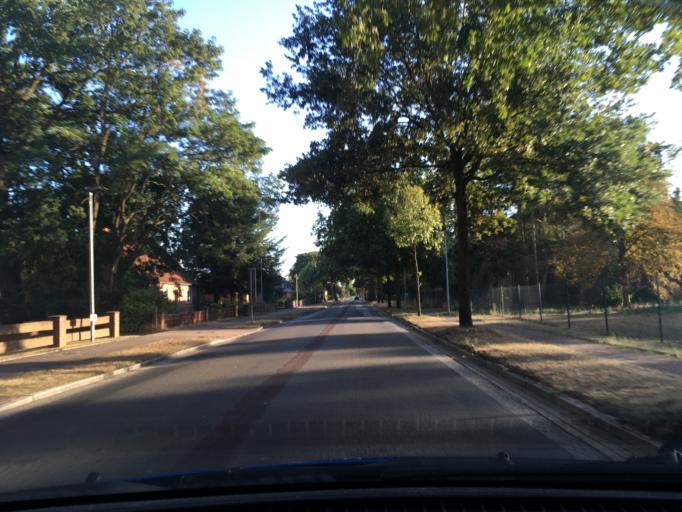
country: DE
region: Mecklenburg-Vorpommern
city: Neu Kaliss
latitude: 53.1876
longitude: 11.2978
